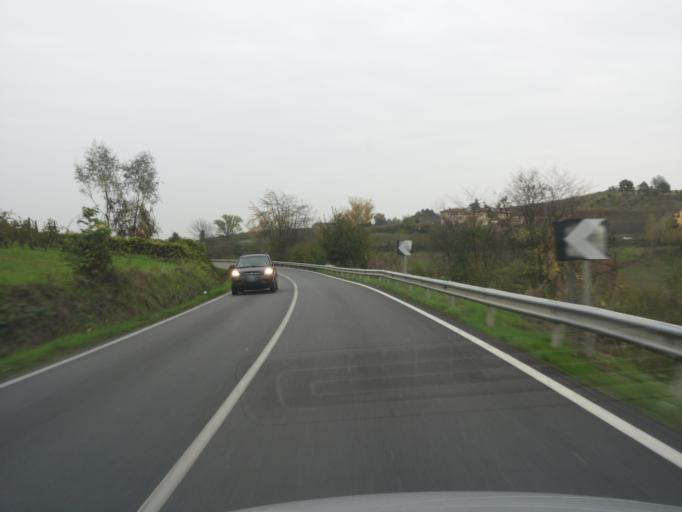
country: IT
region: Piedmont
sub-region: Provincia di Alessandria
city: San Giorgio Monferrato
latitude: 45.1003
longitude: 8.4297
